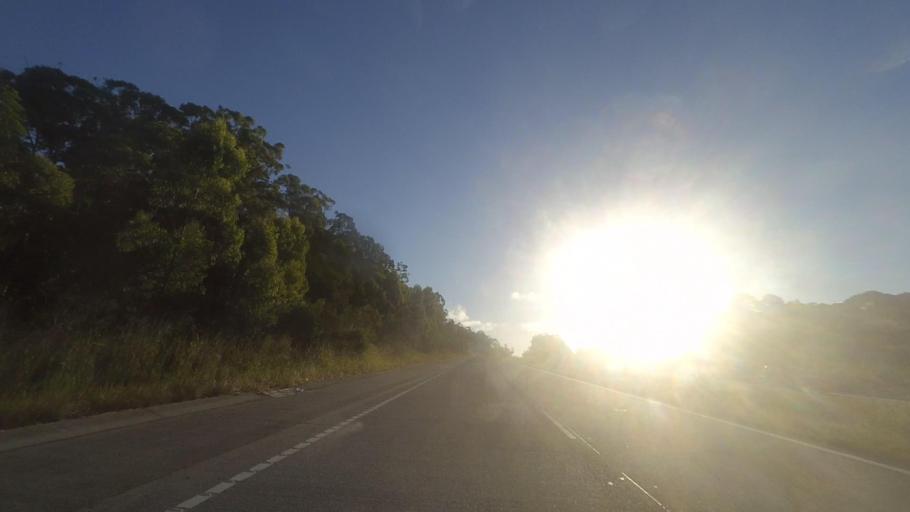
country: AU
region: New South Wales
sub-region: Great Lakes
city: Bulahdelah
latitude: -32.5327
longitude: 152.1823
